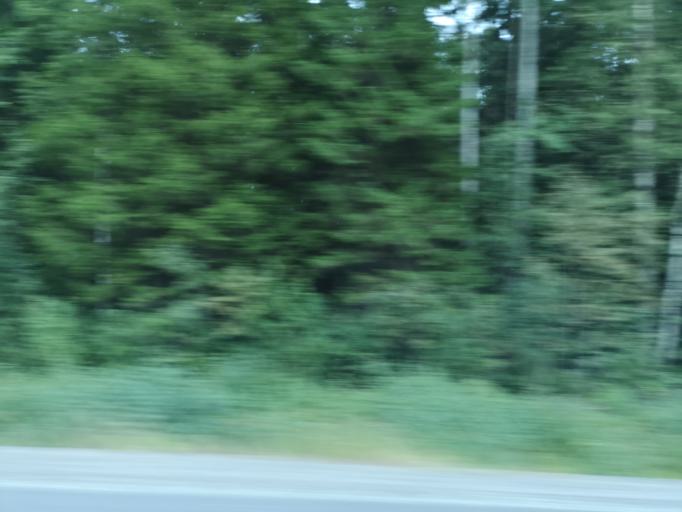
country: FI
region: Central Finland
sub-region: Jyvaeskylae
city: Toivakka
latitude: 62.0649
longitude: 26.0457
